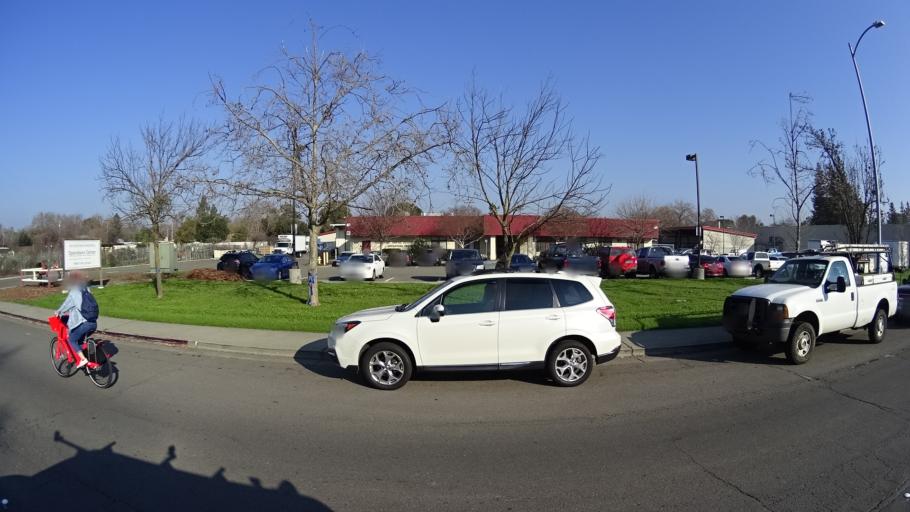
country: US
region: California
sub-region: Yolo County
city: Davis
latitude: 38.5488
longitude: -121.7284
